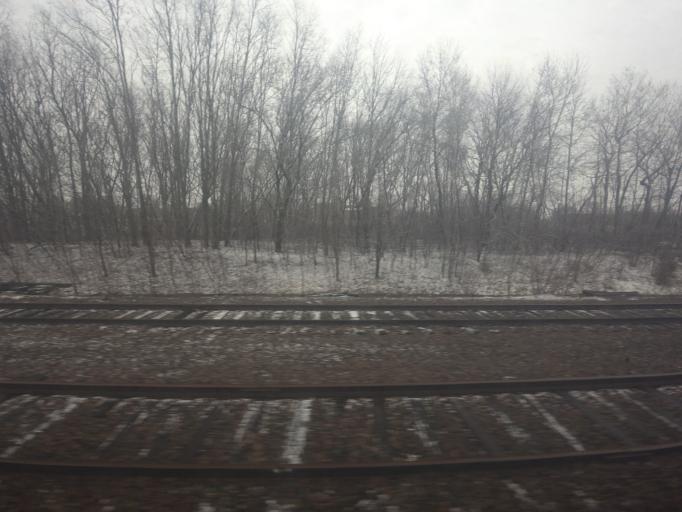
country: CA
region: Ontario
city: Brockville
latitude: 44.5951
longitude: -75.6886
